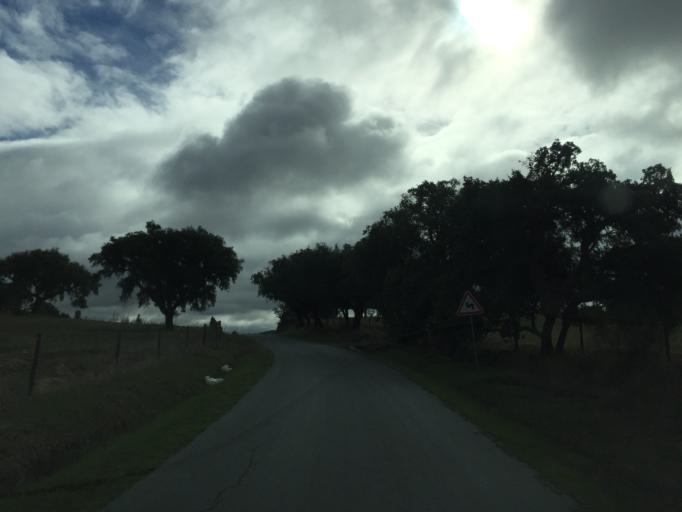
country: PT
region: Portalegre
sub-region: Alter do Chao
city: Alter do Chao
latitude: 39.2333
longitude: -7.6868
